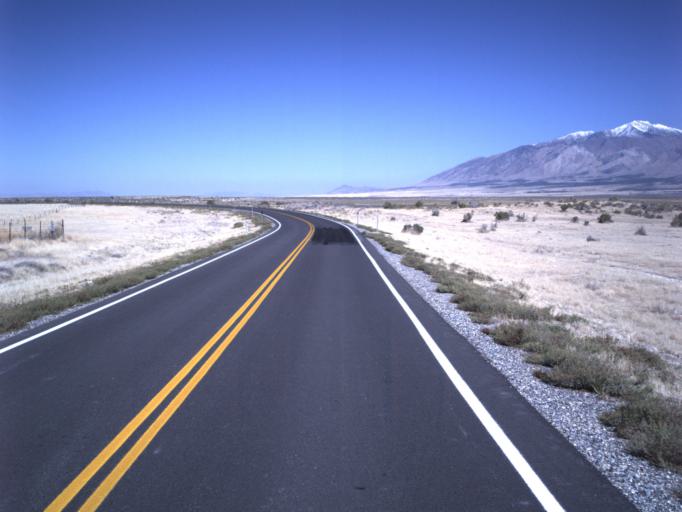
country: US
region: Utah
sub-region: Tooele County
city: Grantsville
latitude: 40.2437
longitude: -112.7231
